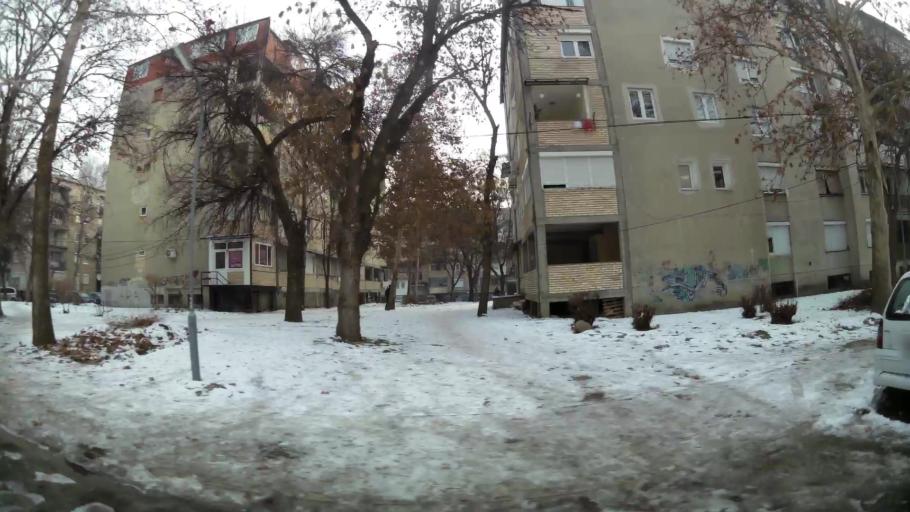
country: MK
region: Cair
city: Cair
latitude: 42.0191
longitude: 21.4455
